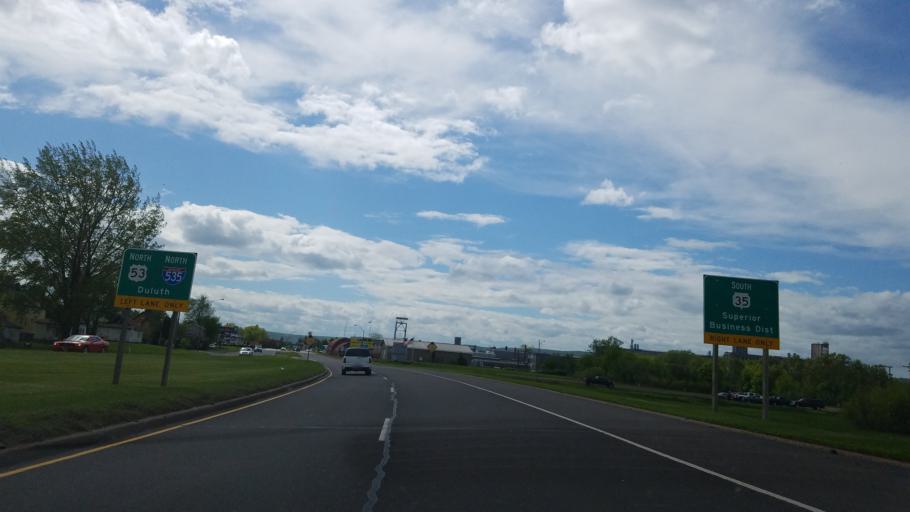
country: US
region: Wisconsin
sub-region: Douglas County
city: Superior
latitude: 46.7336
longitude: -92.0878
